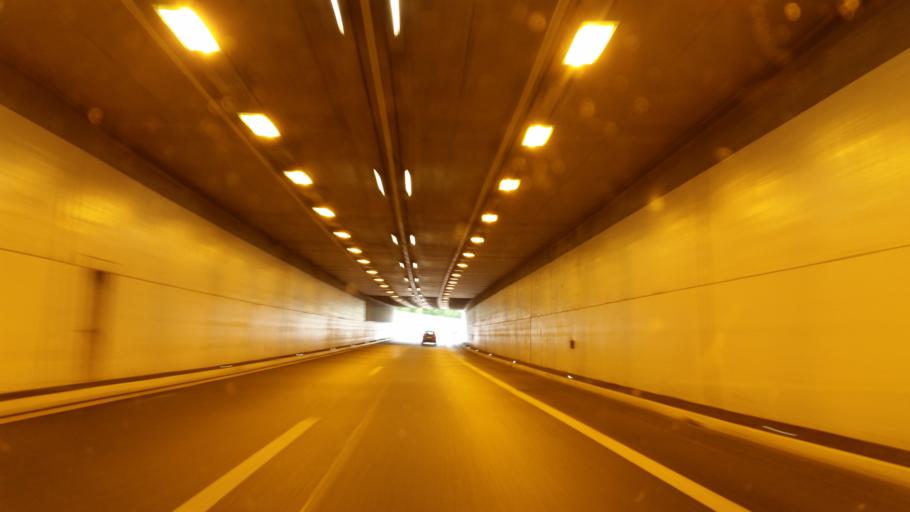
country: CH
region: Neuchatel
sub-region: Boudry District
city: Auvernier
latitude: 46.9755
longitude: 6.8806
